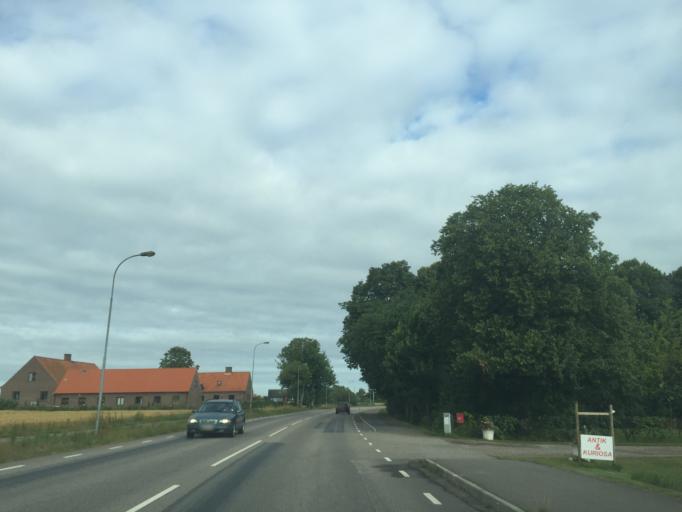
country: SE
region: Skane
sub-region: Angelholms Kommun
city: AEngelholm
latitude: 56.2282
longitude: 12.8851
